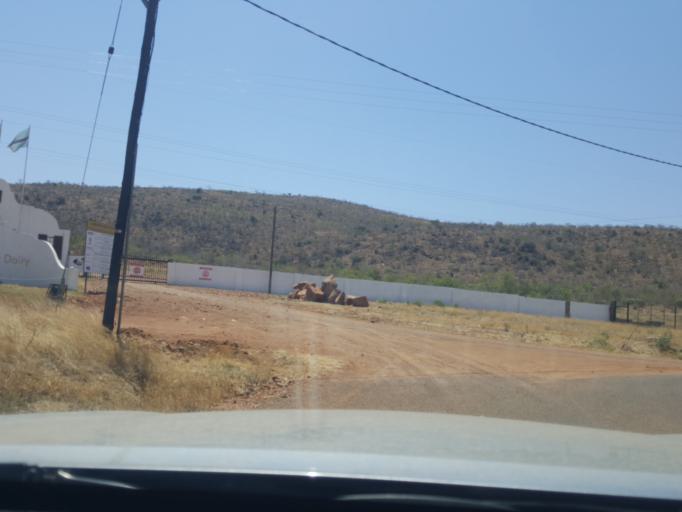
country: BW
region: South East
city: Lobatse
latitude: -25.1912
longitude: 25.6732
